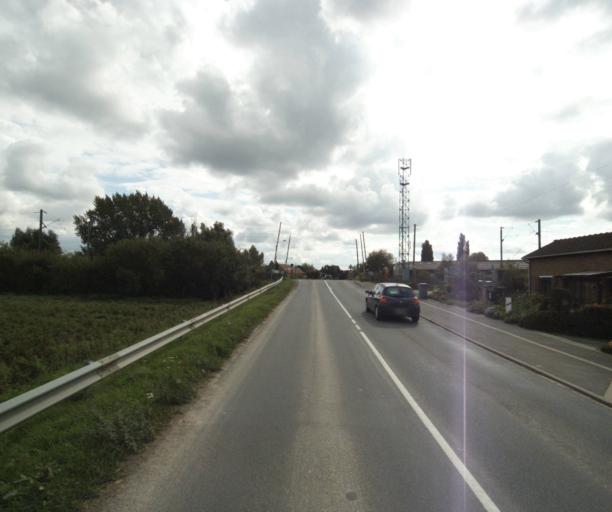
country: FR
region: Nord-Pas-de-Calais
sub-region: Departement du Nord
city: Premesques
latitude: 50.6716
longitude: 2.9483
